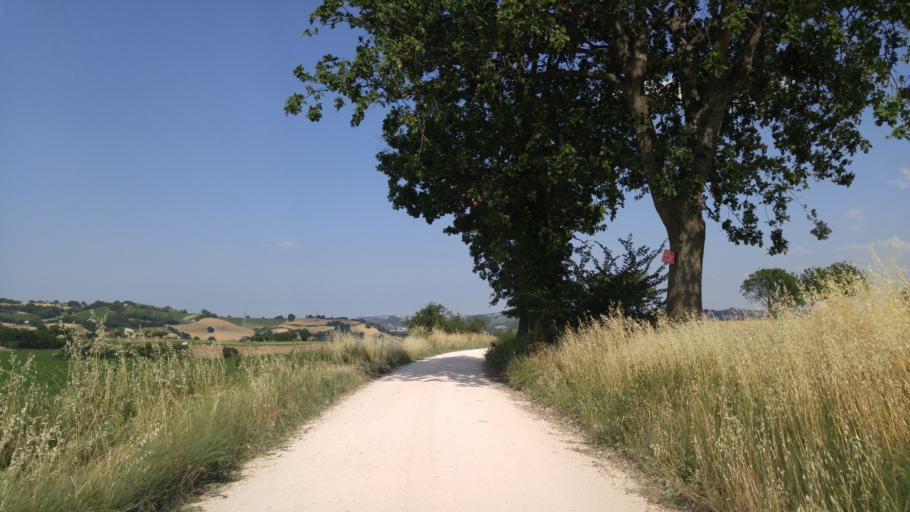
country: IT
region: The Marches
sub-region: Provincia di Pesaro e Urbino
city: Montefelcino
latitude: 43.7277
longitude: 12.8506
